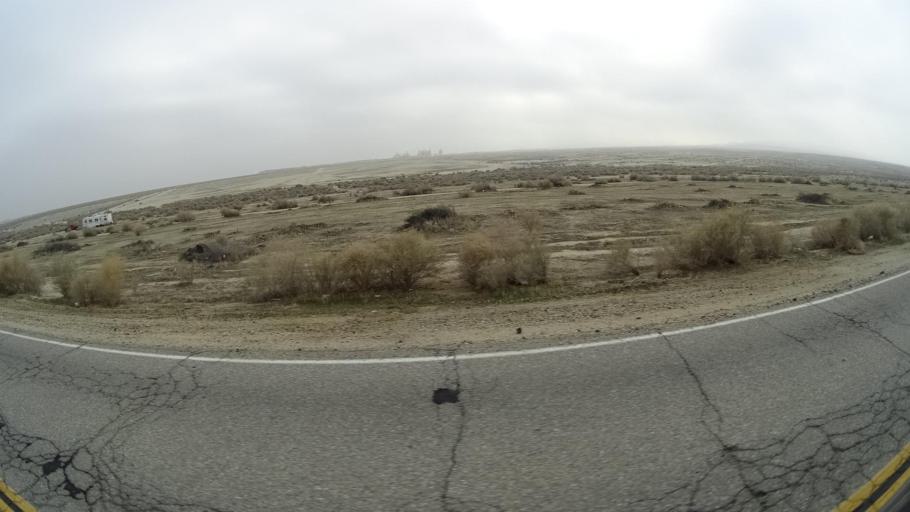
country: US
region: California
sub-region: Kern County
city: South Taft
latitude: 35.1305
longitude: -119.3951
